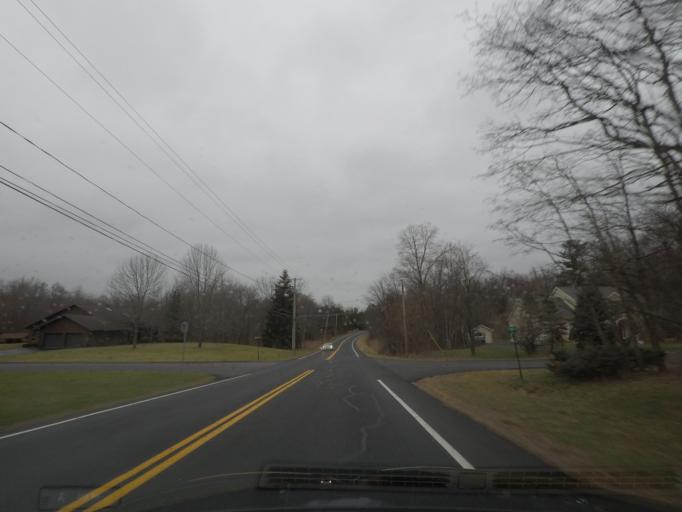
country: US
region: New York
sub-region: Rensselaer County
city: East Greenbush
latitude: 42.6118
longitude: -73.6685
